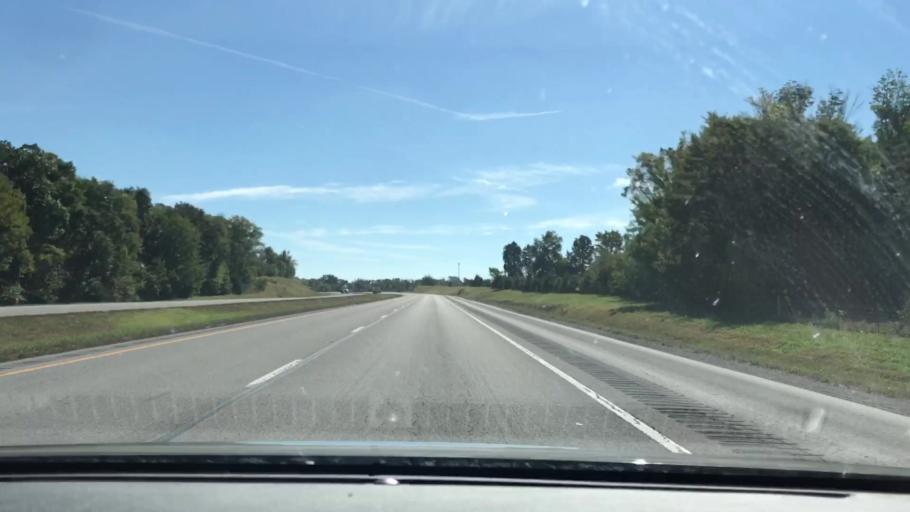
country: US
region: Kentucky
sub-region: Todd County
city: Elkton
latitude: 36.8294
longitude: -87.2255
